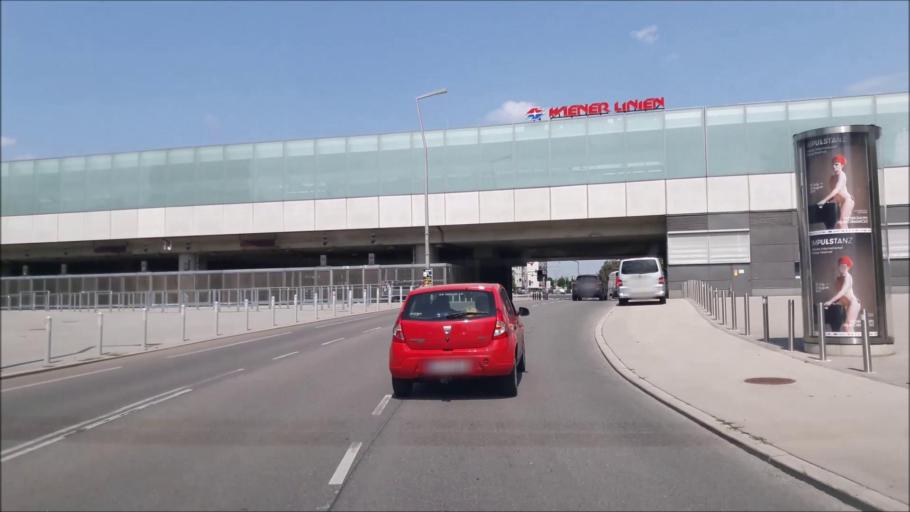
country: AT
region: Vienna
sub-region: Wien Stadt
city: Vienna
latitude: 48.2099
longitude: 16.4201
